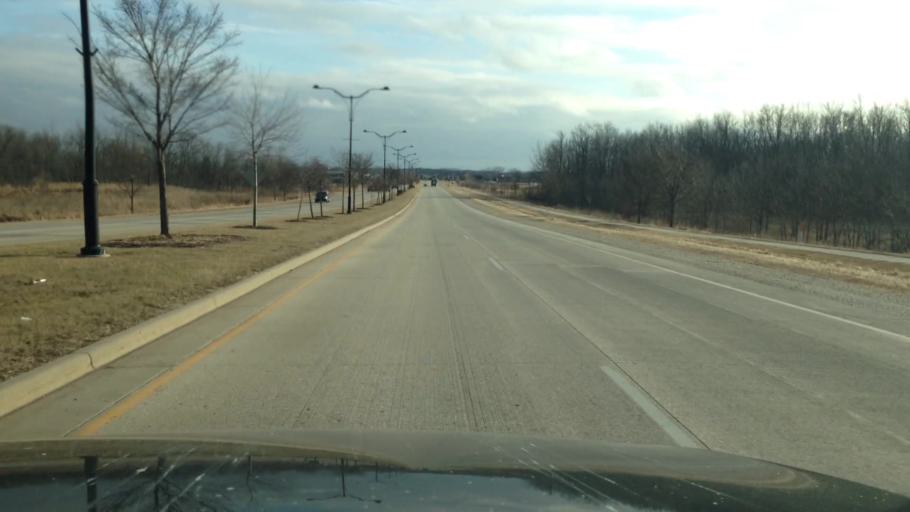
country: US
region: Wisconsin
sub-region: Waukesha County
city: Muskego
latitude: 42.9255
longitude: -88.1131
